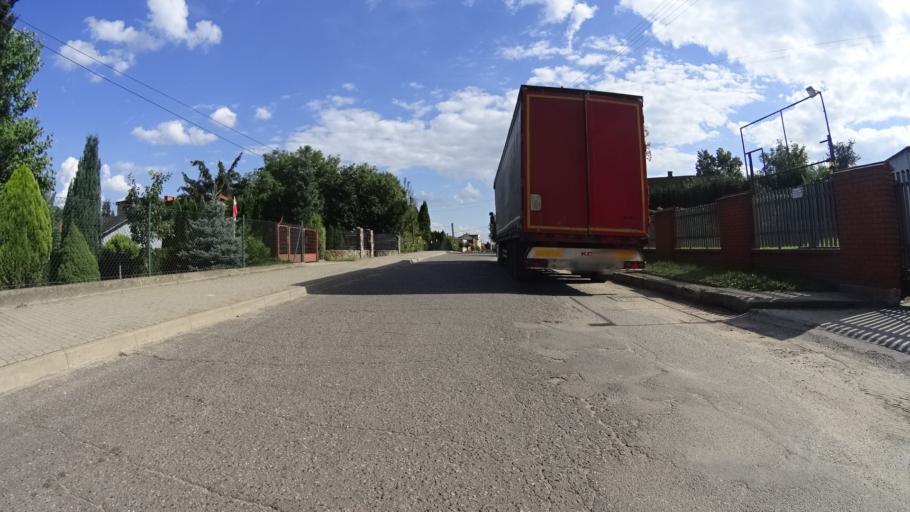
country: PL
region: Masovian Voivodeship
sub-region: Powiat grojecki
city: Mogielnica
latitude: 51.6982
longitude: 20.7160
